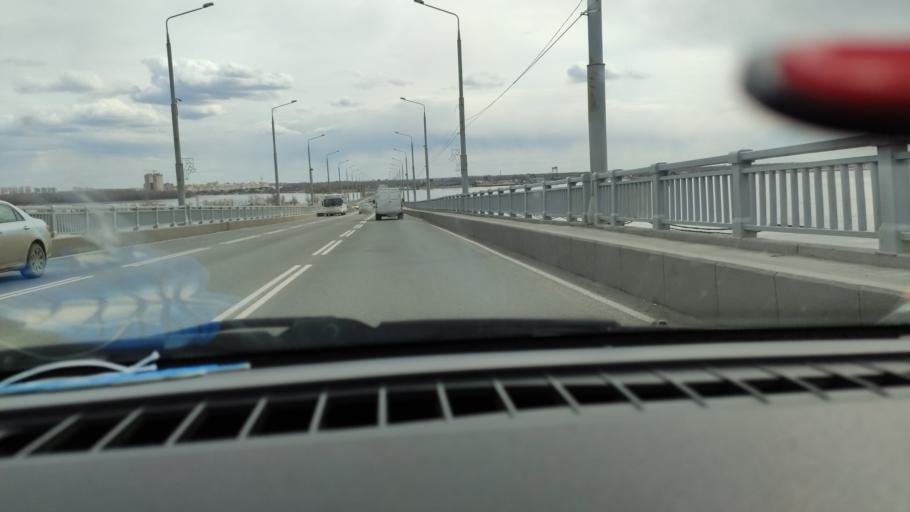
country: RU
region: Saratov
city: Engel's
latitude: 51.5182
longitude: 46.0697
